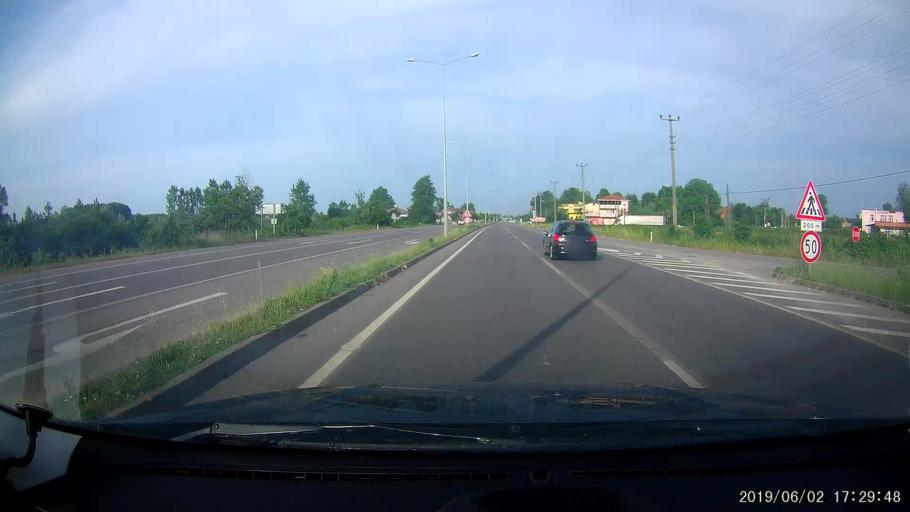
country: TR
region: Samsun
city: Carsamba
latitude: 41.2133
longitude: 36.7667
